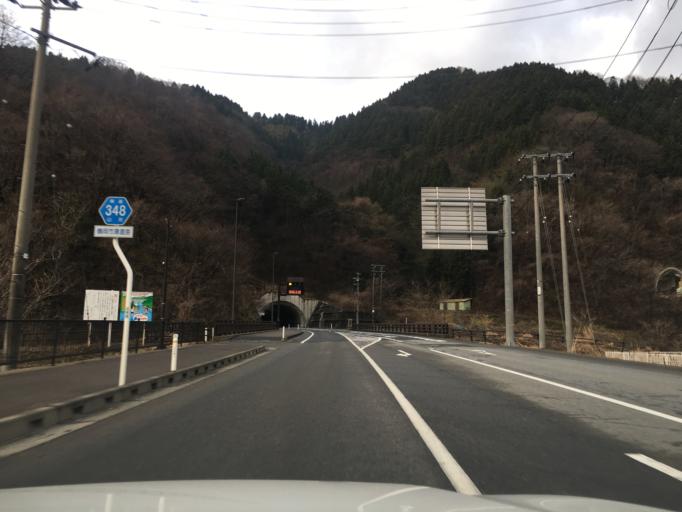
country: JP
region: Yamagata
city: Tsuruoka
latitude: 38.6158
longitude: 139.5950
